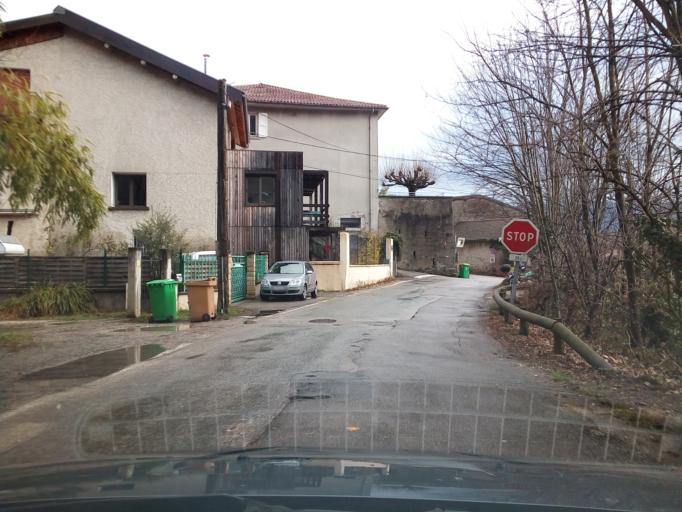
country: FR
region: Rhone-Alpes
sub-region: Departement de l'Isere
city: Corenc
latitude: 45.2163
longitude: 5.7539
